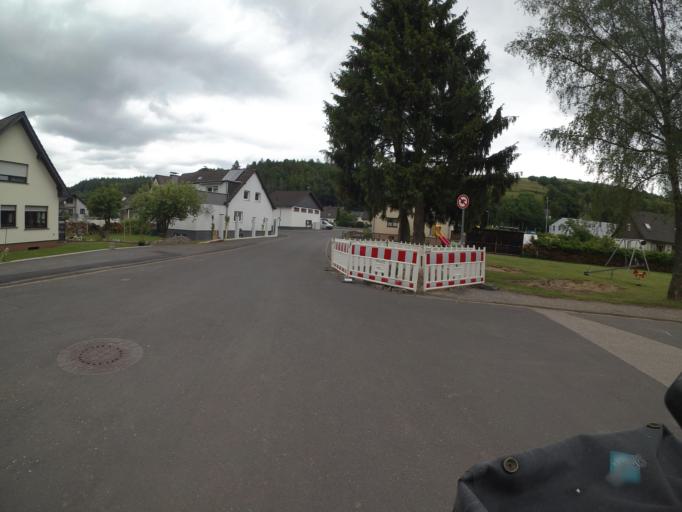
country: DE
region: North Rhine-Westphalia
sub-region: Regierungsbezirk Koln
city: Schleiden
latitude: 50.5120
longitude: 6.4648
